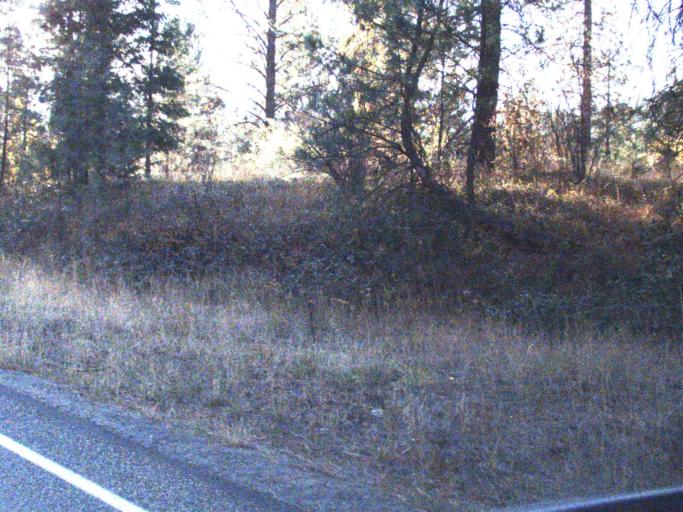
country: CA
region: British Columbia
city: Rossland
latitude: 48.8783
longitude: -117.8369
